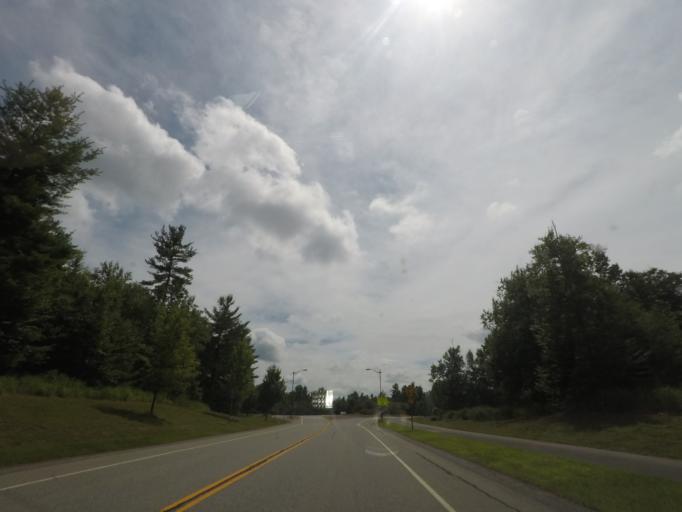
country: US
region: New York
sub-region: Saratoga County
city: Country Knolls
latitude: 42.9570
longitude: -73.7606
